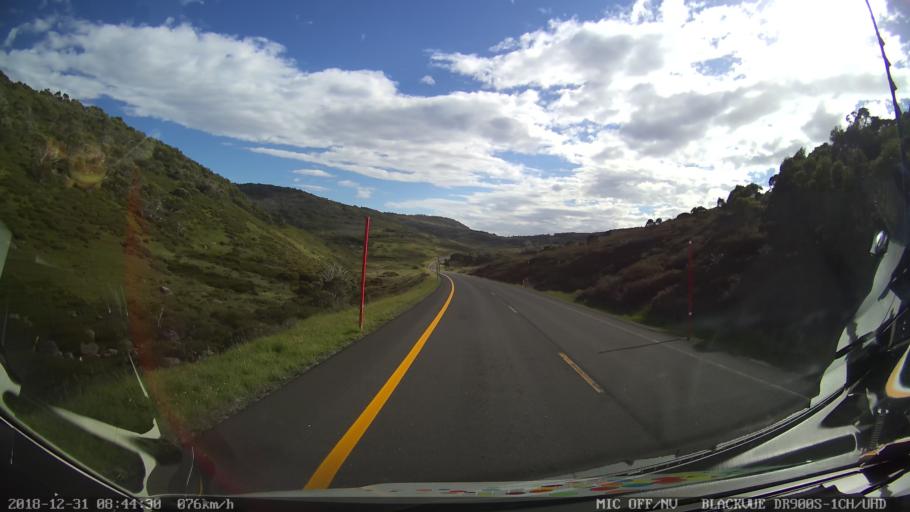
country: AU
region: New South Wales
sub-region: Snowy River
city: Jindabyne
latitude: -36.3831
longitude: 148.4552
